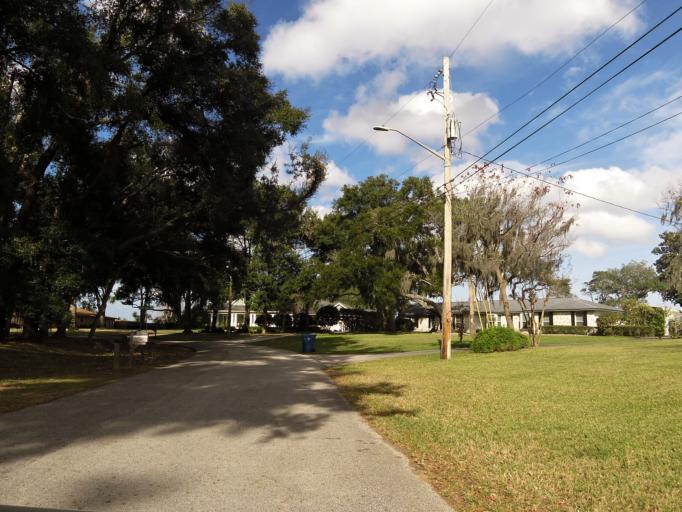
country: US
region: Florida
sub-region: Duval County
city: Atlantic Beach
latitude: 30.3596
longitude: -81.4626
